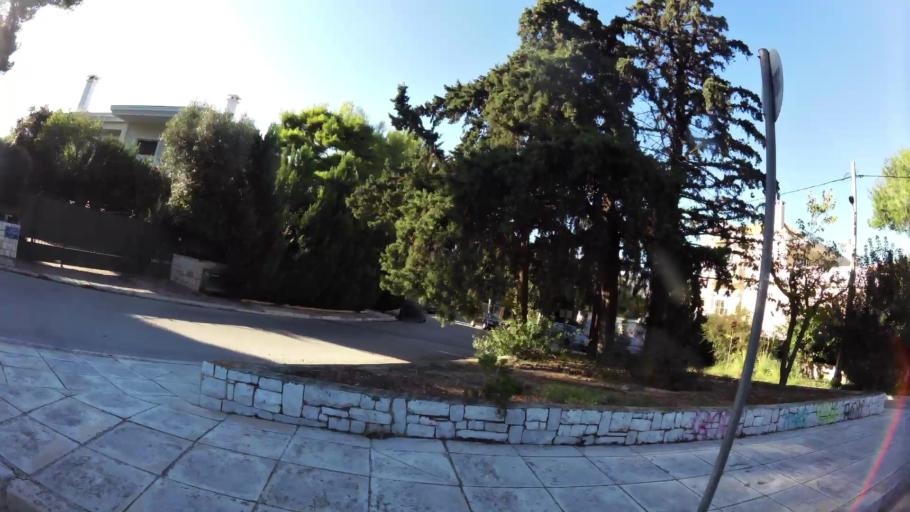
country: GR
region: Attica
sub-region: Nomarchia Athinas
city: Ekali
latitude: 38.1060
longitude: 23.8369
